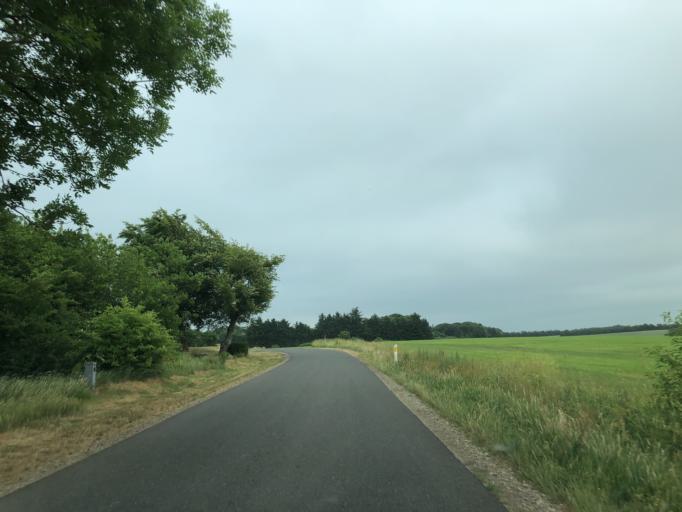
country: DK
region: Central Jutland
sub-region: Holstebro Kommune
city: Holstebro
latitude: 56.2556
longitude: 8.5706
